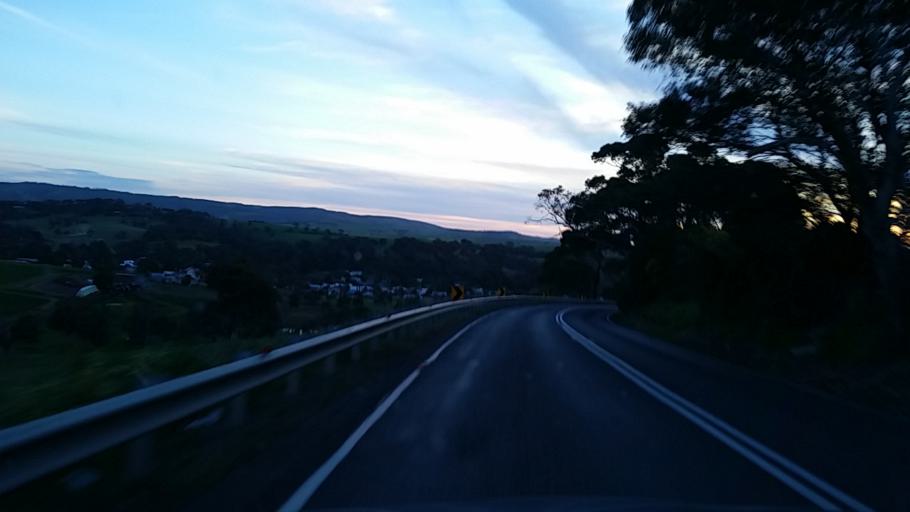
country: AU
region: South Australia
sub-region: Yankalilla
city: Normanville
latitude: -35.4556
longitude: 138.3604
